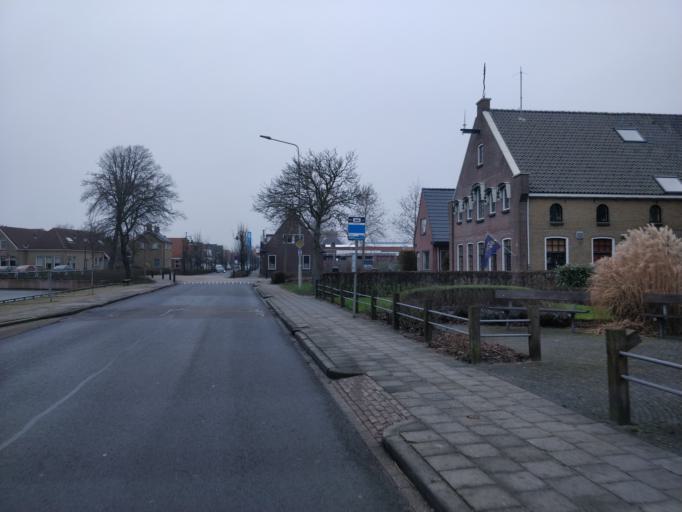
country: NL
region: Friesland
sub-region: Gemeente Het Bildt
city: Sint Annaparochie
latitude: 53.2740
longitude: 5.6577
